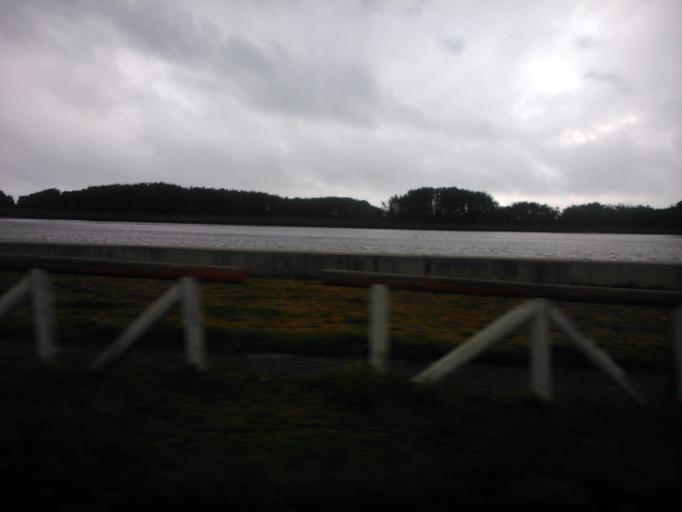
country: CL
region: Araucania
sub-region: Provincia de Cautin
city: Carahue
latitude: -38.8025
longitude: -73.4003
